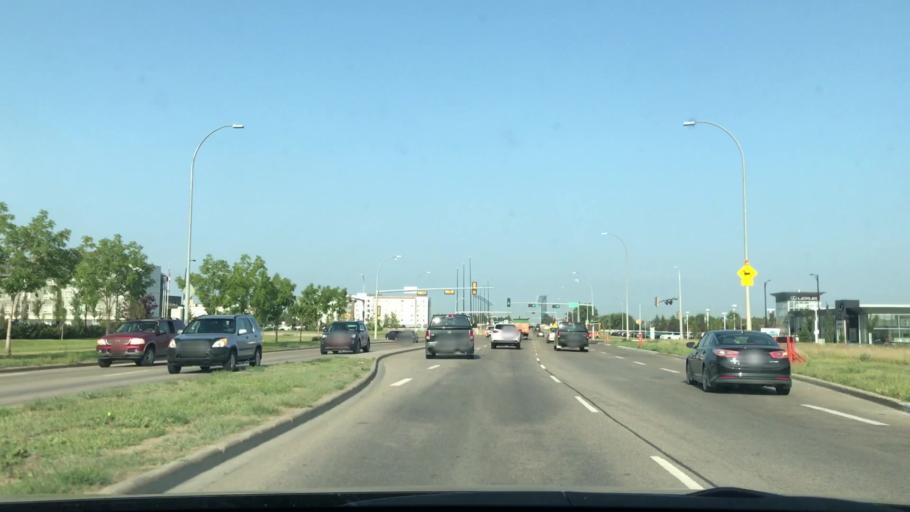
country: CA
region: Alberta
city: Beaumont
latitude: 53.4249
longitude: -113.4872
